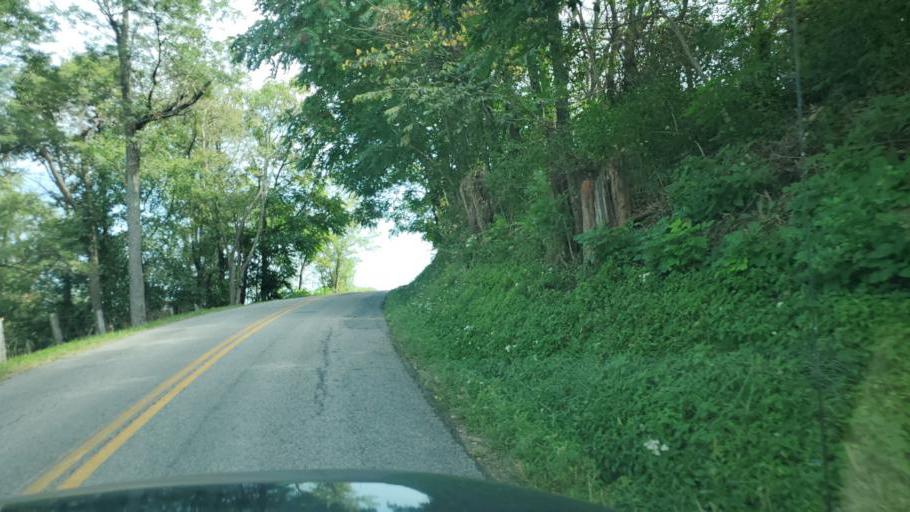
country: US
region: Ohio
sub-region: Muskingum County
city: Zanesville
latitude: 39.9421
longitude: -82.1158
